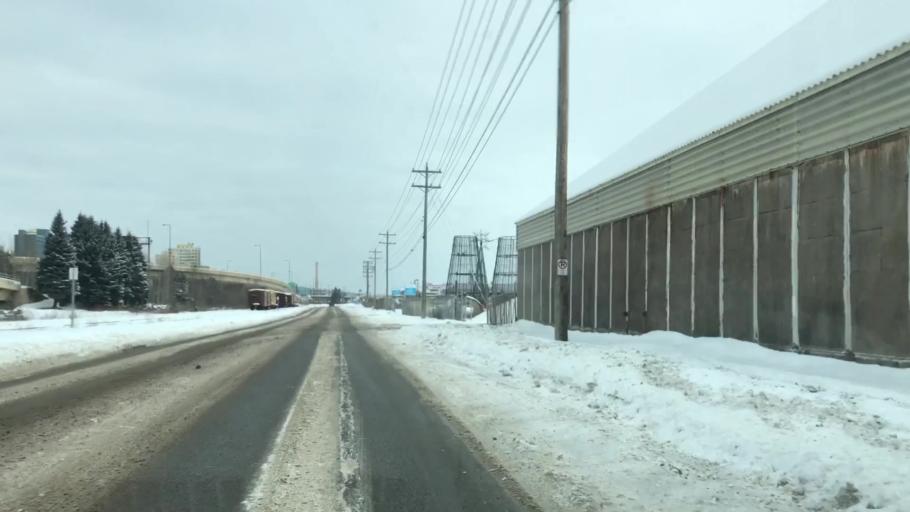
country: US
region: Minnesota
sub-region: Saint Louis County
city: Duluth
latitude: 46.7753
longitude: -92.1091
